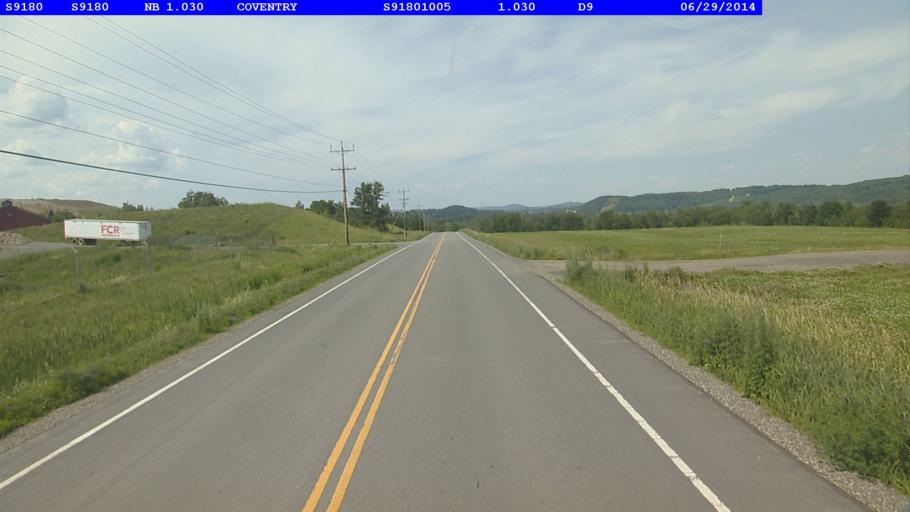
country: US
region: Vermont
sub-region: Orleans County
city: Newport
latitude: 44.9035
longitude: -72.2231
